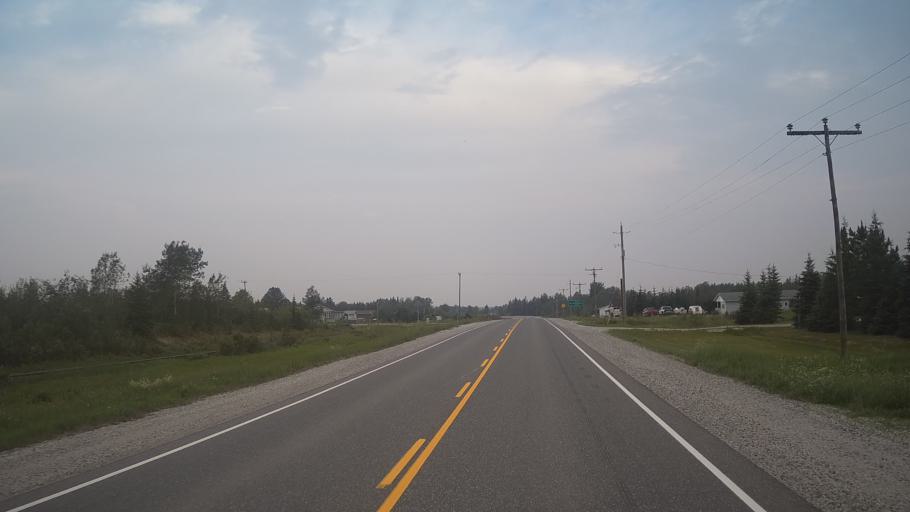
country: CA
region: Ontario
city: Hearst
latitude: 49.6681
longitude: -83.5043
